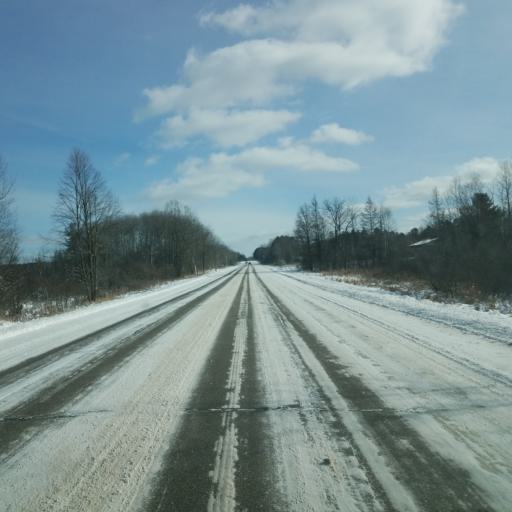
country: US
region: Michigan
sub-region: Osceola County
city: Evart
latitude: 43.9008
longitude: -85.1361
